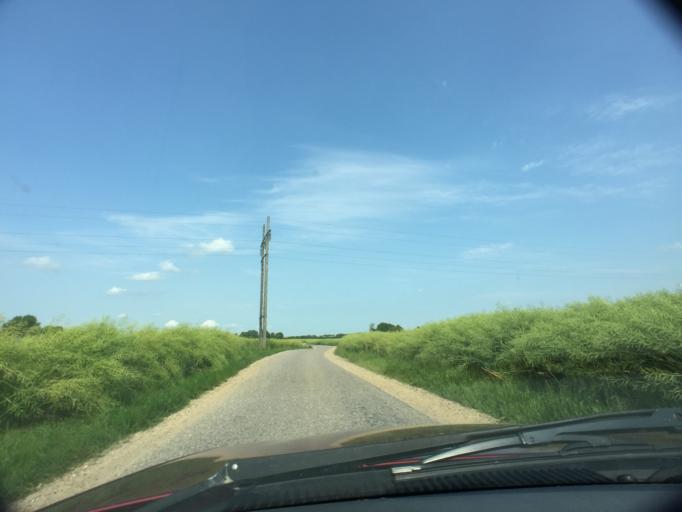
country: DK
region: Central Jutland
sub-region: Favrskov Kommune
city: Hammel
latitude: 56.2448
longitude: 9.7509
